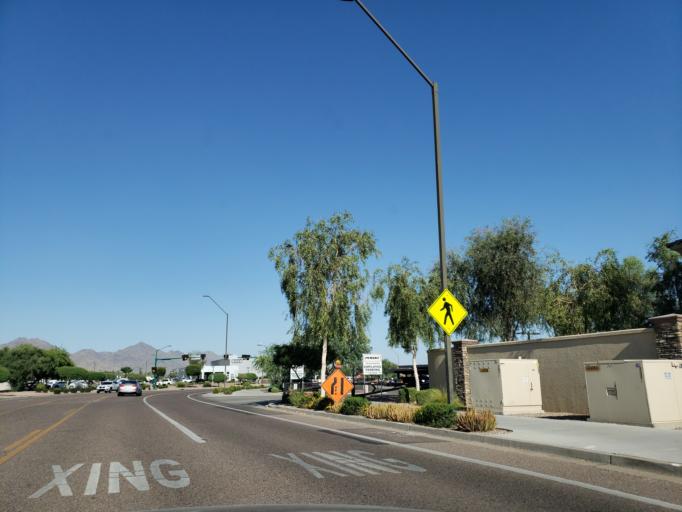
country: US
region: Arizona
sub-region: Maricopa County
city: Paradise Valley
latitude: 33.6477
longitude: -111.9291
